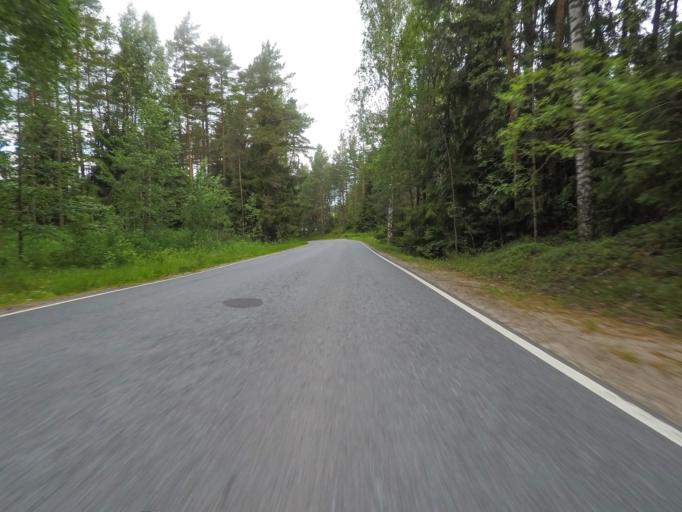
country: FI
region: Varsinais-Suomi
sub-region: Salo
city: Muurla
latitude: 60.3392
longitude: 23.2995
